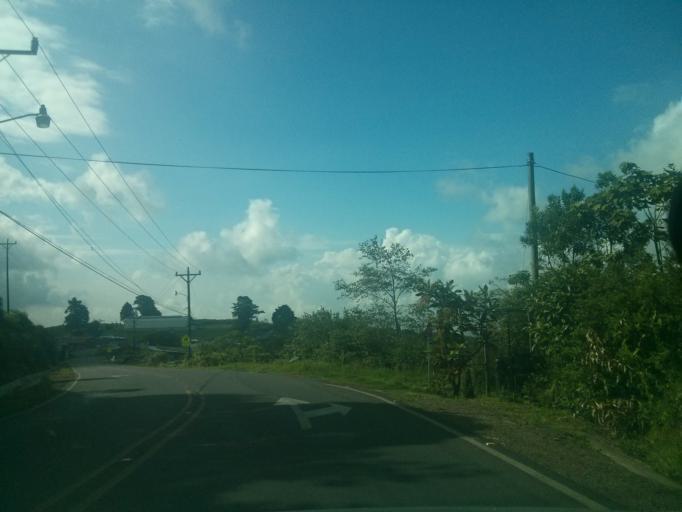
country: CR
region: Heredia
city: Santo Domingo
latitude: 10.1703
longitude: -84.1574
